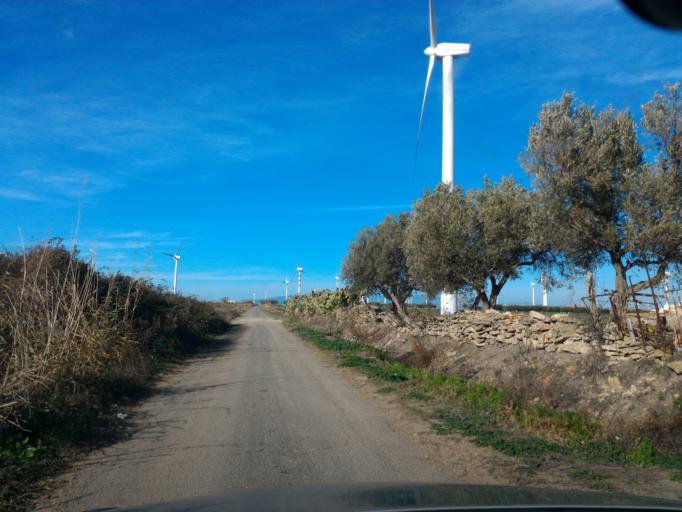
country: IT
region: Calabria
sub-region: Provincia di Crotone
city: Isola di Capo Rizzuto
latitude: 38.9448
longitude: 17.0531
